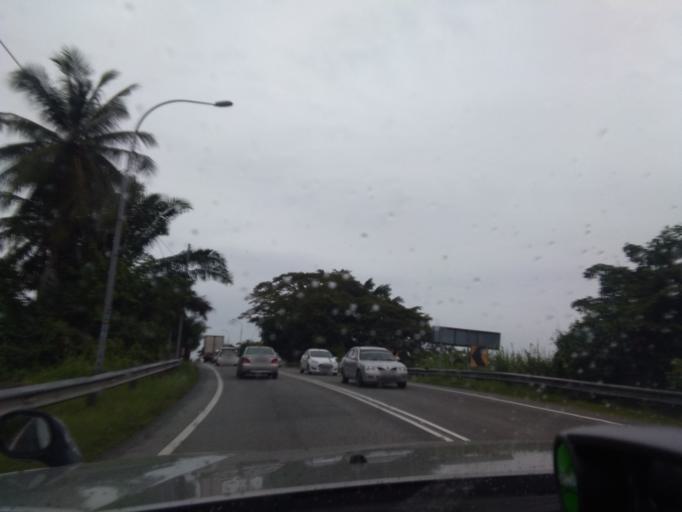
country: MY
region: Penang
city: Nibong Tebal
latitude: 5.1627
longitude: 100.4789
